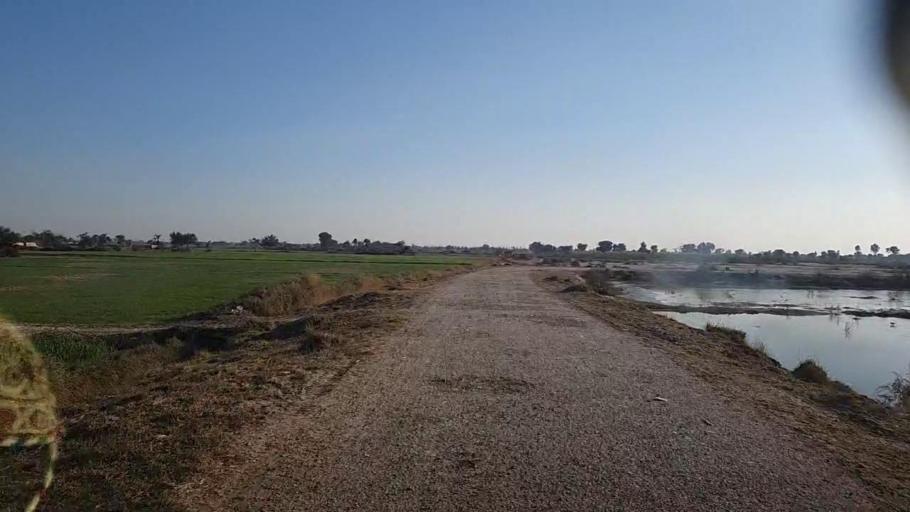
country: PK
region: Sindh
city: Khairpur
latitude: 28.0188
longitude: 69.7108
